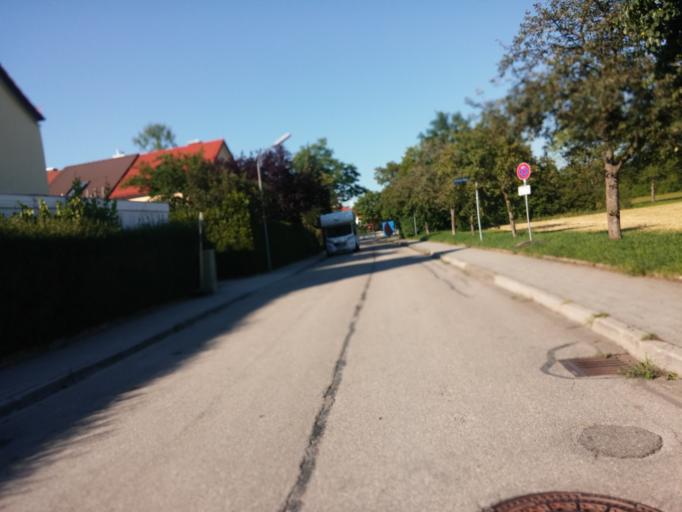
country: DE
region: Bavaria
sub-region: Upper Bavaria
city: Vaterstetten
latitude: 48.1086
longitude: 11.7765
